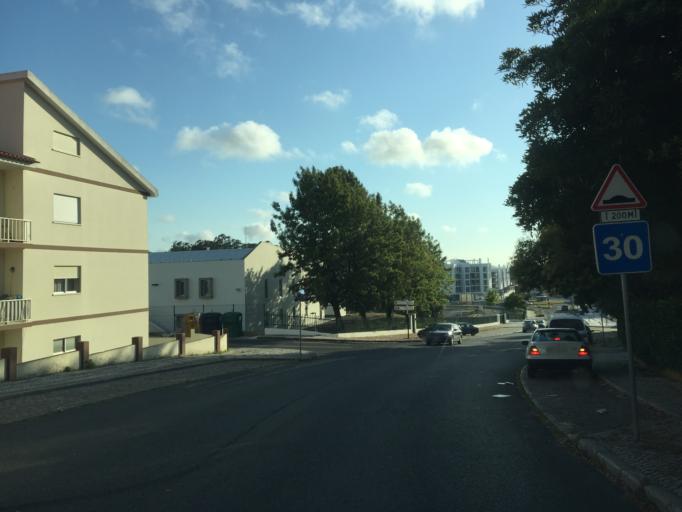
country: PT
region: Leiria
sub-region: Caldas da Rainha
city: Caldas da Rainha
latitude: 39.3981
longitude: -9.1308
